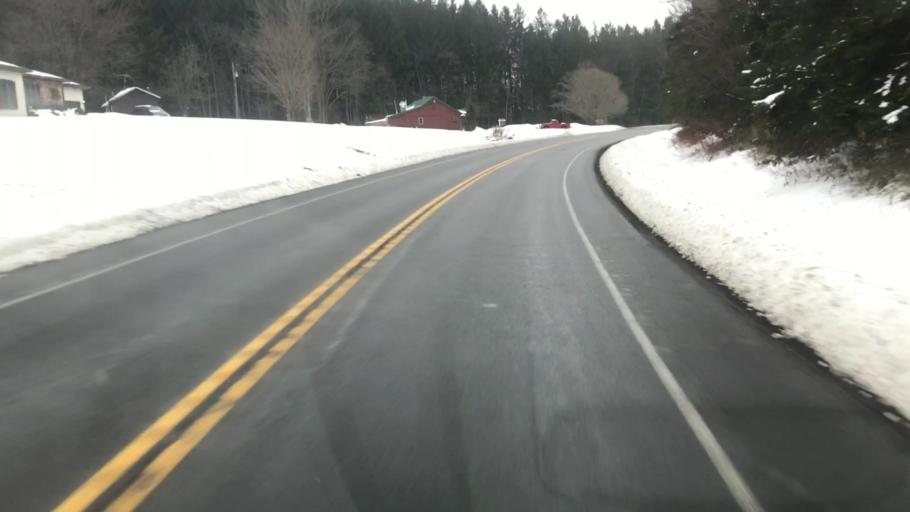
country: US
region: New York
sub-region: Cayuga County
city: Moravia
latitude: 42.7487
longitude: -76.3198
